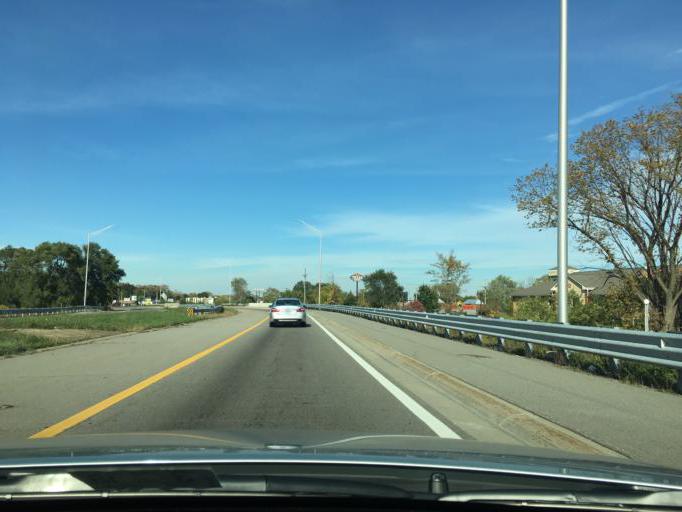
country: US
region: Michigan
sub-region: Macomb County
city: Roseville
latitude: 42.5233
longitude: -82.9162
